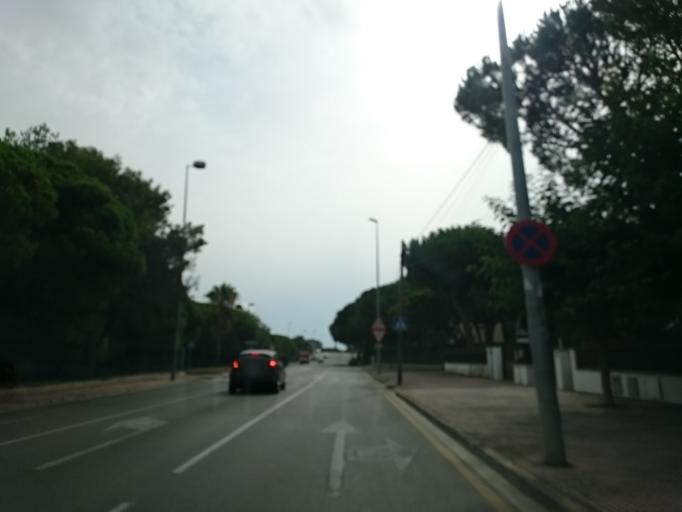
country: ES
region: Catalonia
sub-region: Provincia de Barcelona
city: Gava
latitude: 41.2692
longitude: 2.0170
